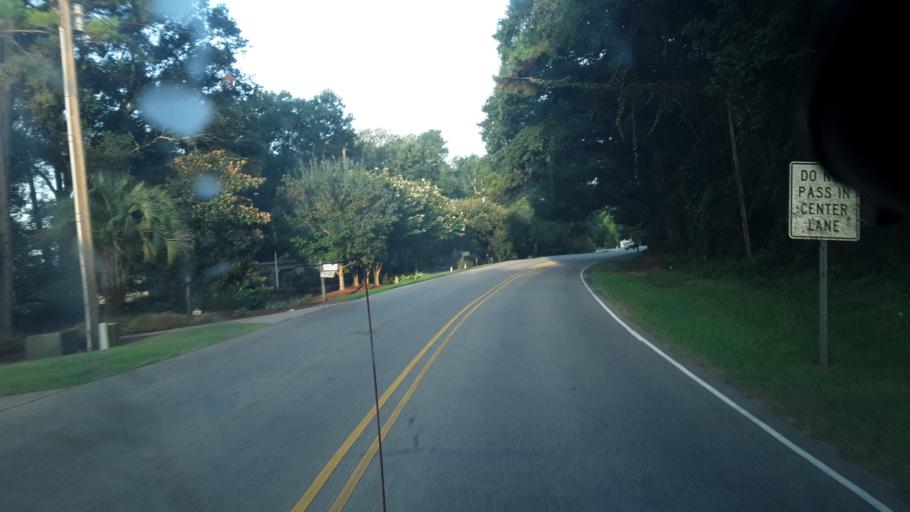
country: US
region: North Carolina
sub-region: Brunswick County
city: Sunset Beach
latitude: 33.8788
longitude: -78.5376
